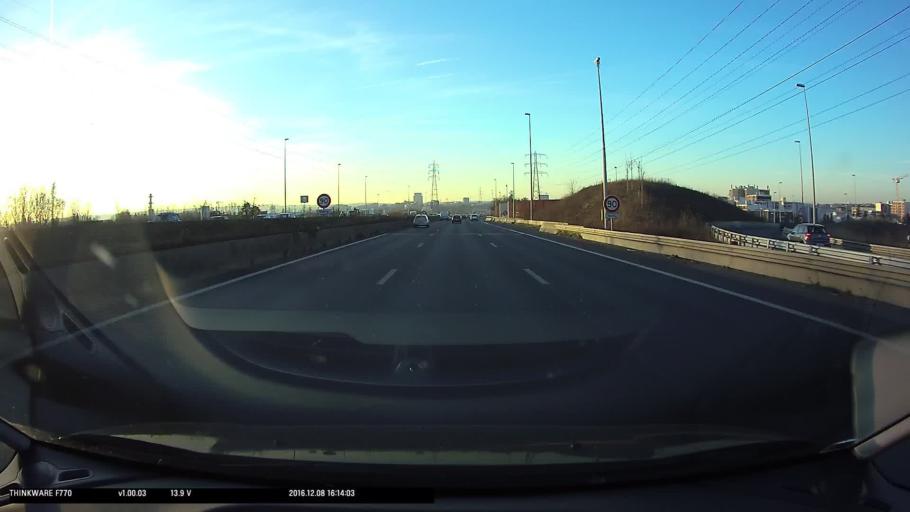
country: FR
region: Ile-de-France
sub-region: Departement du Val-d'Oise
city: Saint-Ouen-l'Aumone
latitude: 49.0323
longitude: 2.1126
